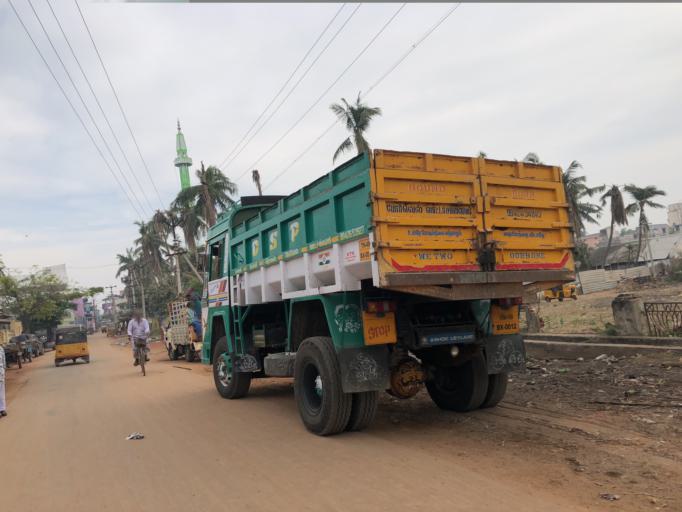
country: IN
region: Tamil Nadu
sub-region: Thanjavur
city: Adirampattinam
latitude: 10.3391
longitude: 79.3798
